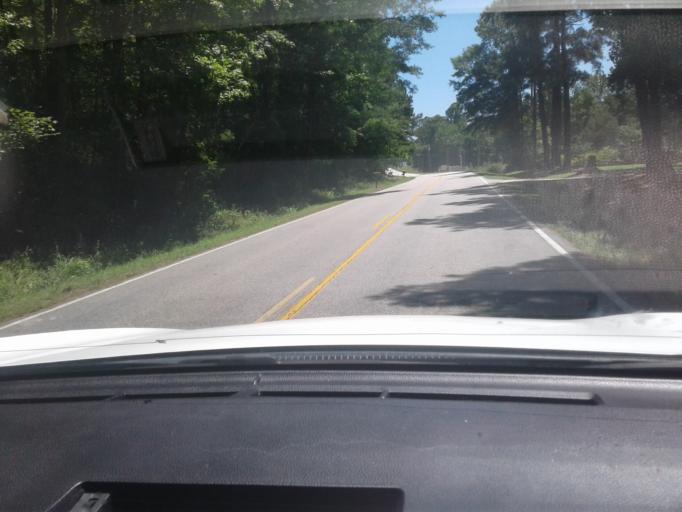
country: US
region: North Carolina
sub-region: Harnett County
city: Erwin
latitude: 35.3215
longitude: -78.7227
